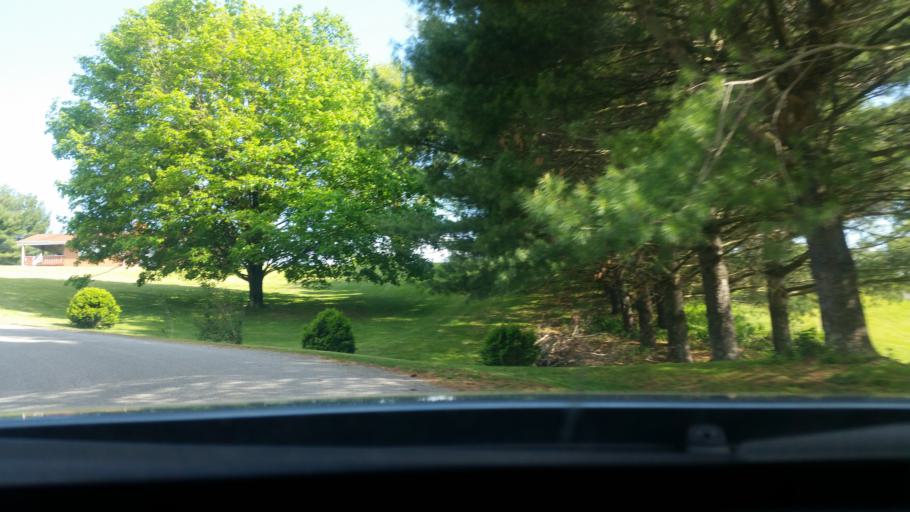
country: US
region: Virginia
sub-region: Giles County
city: Pembroke
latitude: 37.3067
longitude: -80.6371
